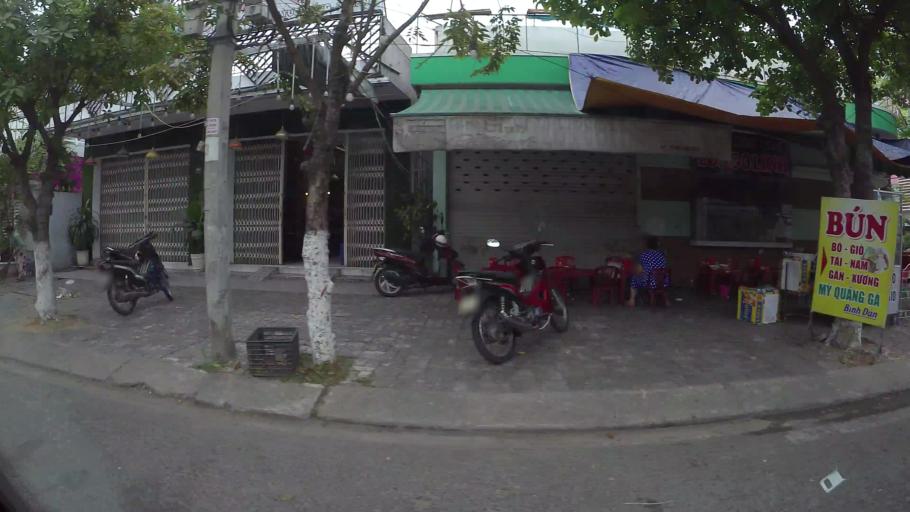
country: VN
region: Da Nang
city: Thanh Khe
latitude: 16.0678
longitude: 108.1880
